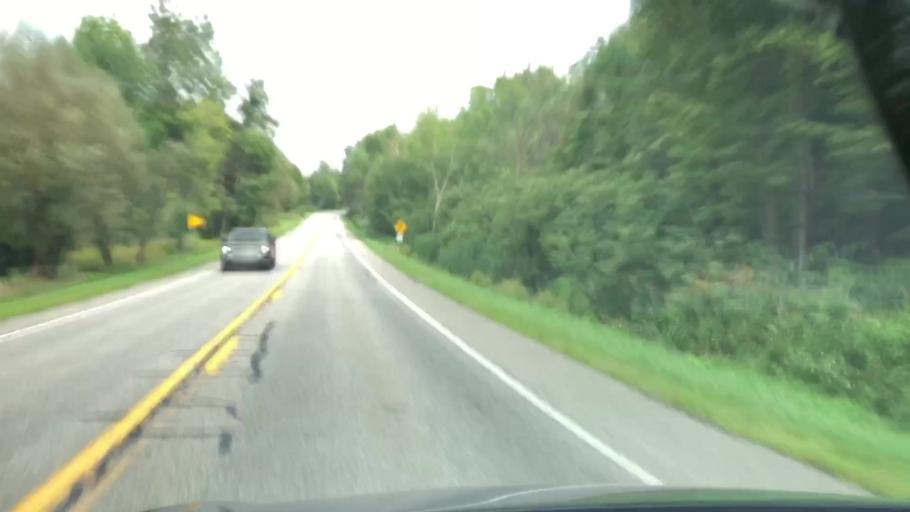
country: US
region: Pennsylvania
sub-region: Erie County
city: Union City
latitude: 42.0528
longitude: -79.8492
